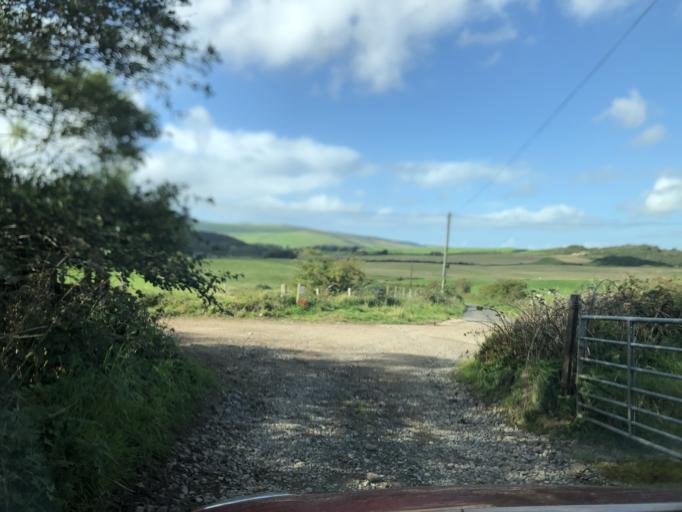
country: GB
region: Scotland
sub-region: Argyll and Bute
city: Campbeltown
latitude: 55.3189
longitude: -5.6145
